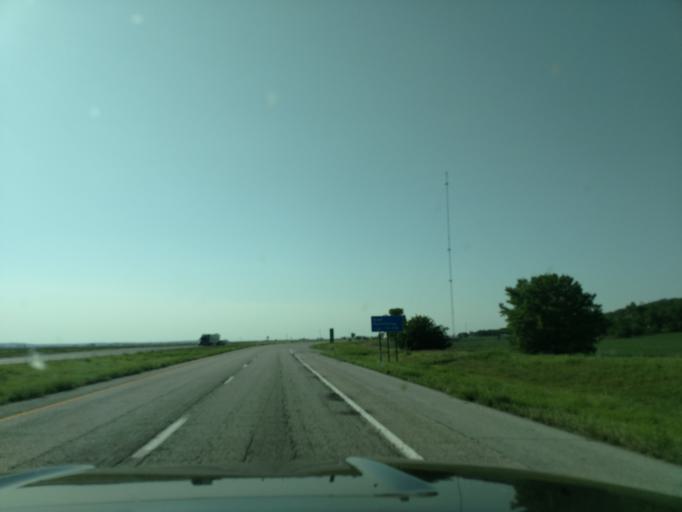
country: US
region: Missouri
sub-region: Atchison County
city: Rock Port
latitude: 40.3702
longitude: -95.5337
